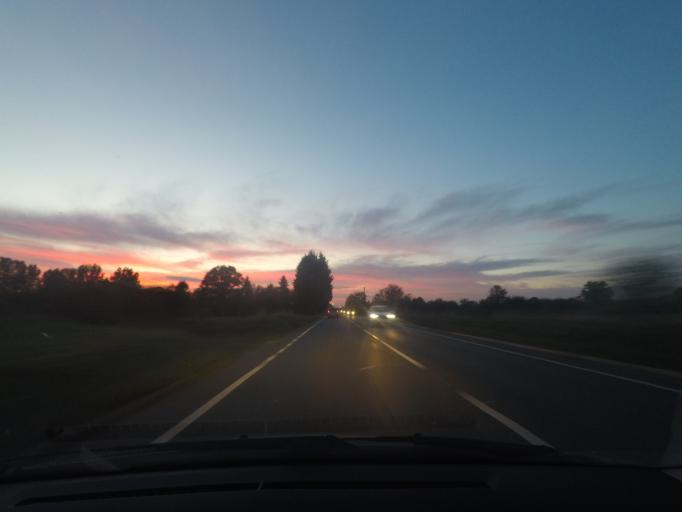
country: GB
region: England
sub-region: East Riding of Yorkshire
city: Thornton
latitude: 53.9312
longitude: -0.8292
